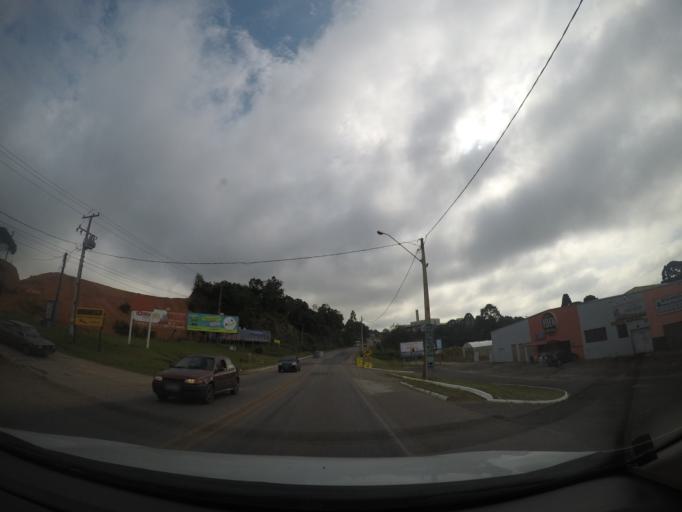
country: BR
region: Parana
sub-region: Colombo
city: Colombo
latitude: -25.3636
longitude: -49.2201
